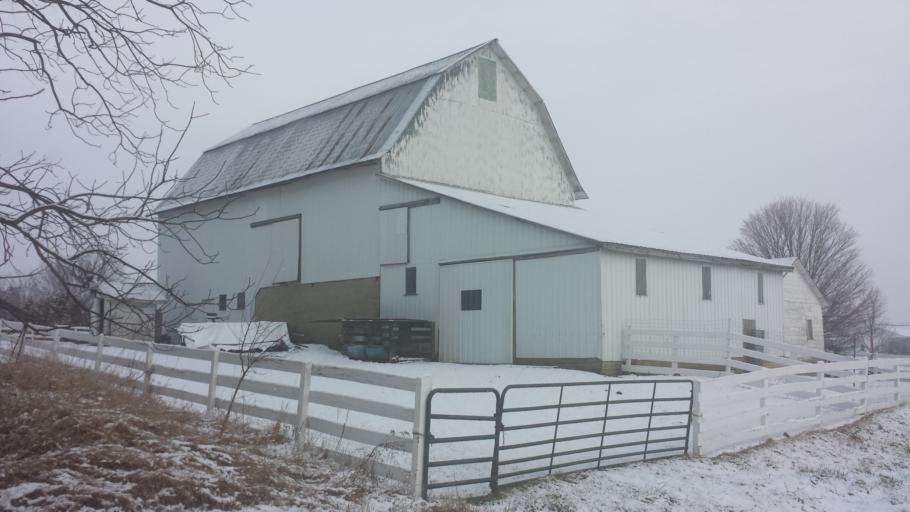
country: US
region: Ohio
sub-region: Knox County
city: Fredericktown
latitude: 40.5247
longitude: -82.6187
